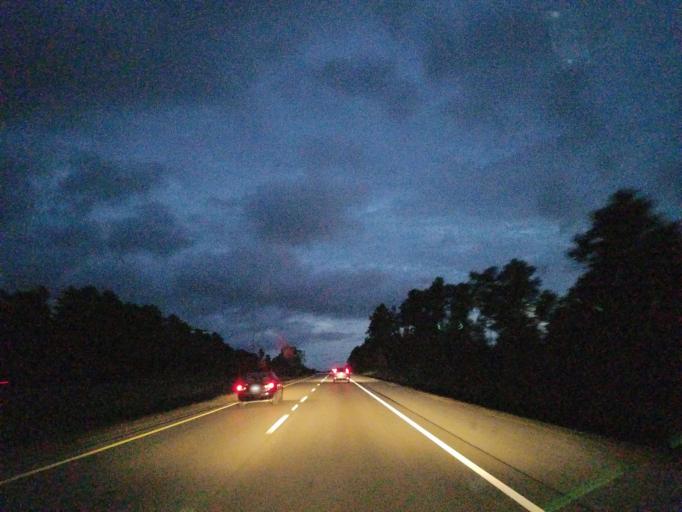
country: US
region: Mississippi
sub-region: Jones County
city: Sharon
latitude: 31.8248
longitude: -89.0516
